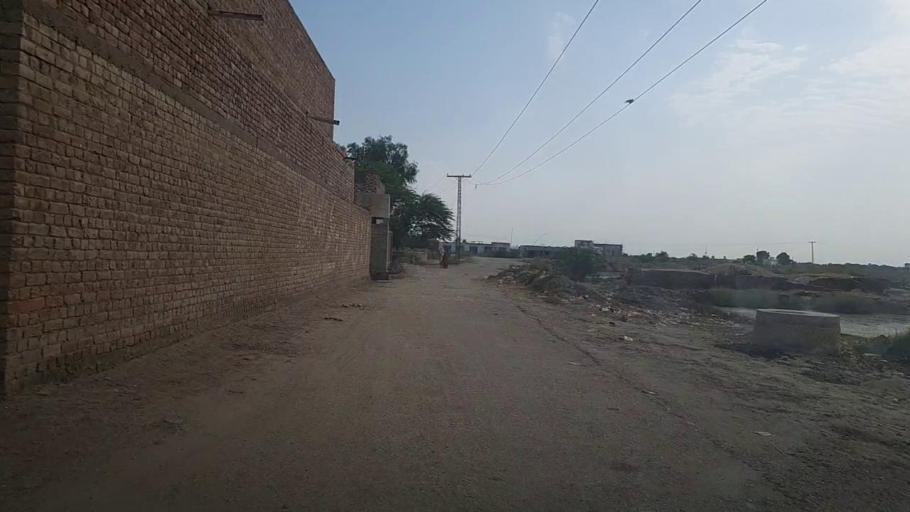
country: PK
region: Sindh
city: Mirpur Mathelo
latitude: 27.9167
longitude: 69.5177
